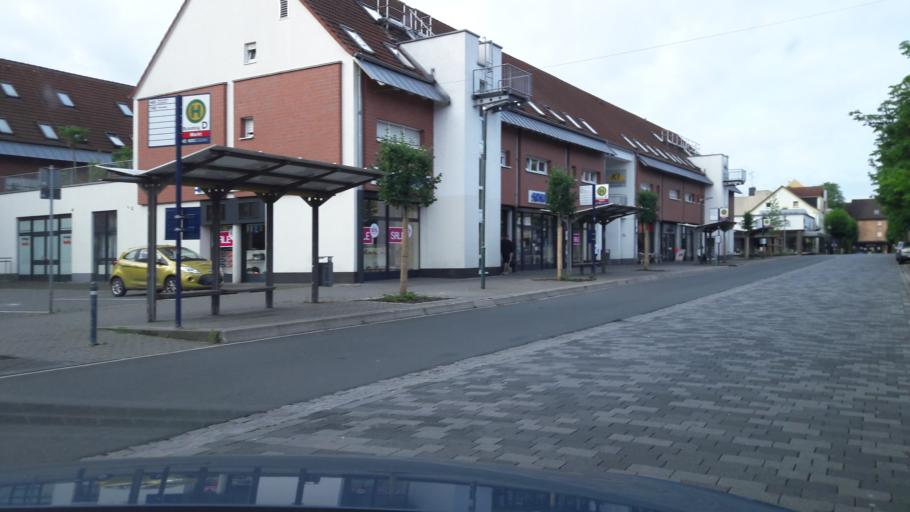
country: DE
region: North Rhine-Westphalia
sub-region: Regierungsbezirk Munster
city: Ennigerloh
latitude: 51.8357
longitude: 8.0275
